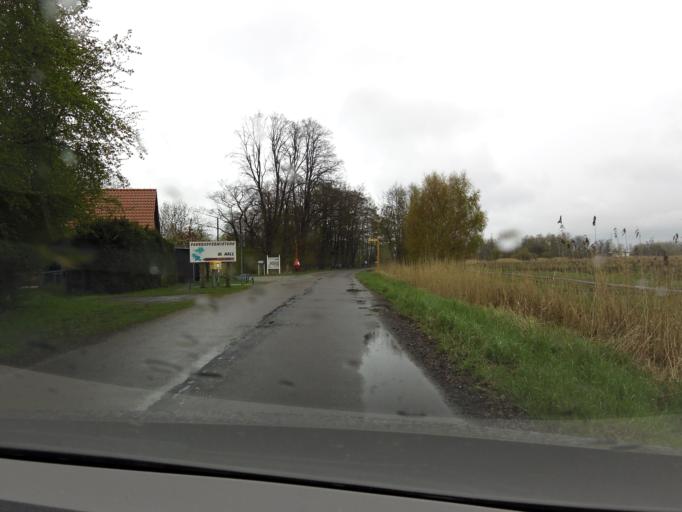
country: DE
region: Mecklenburg-Vorpommern
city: Barth
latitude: 54.4307
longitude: 12.8026
